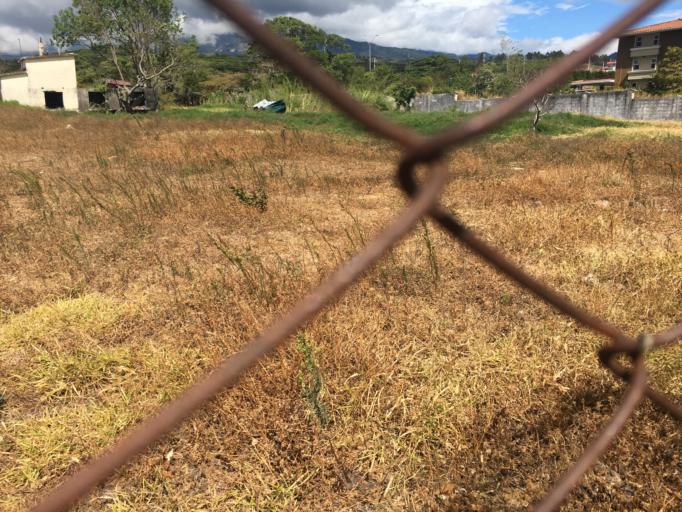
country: PA
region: Chiriqui
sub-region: Distrito Boquete
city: Boquete
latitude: 8.7546
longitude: -82.4307
